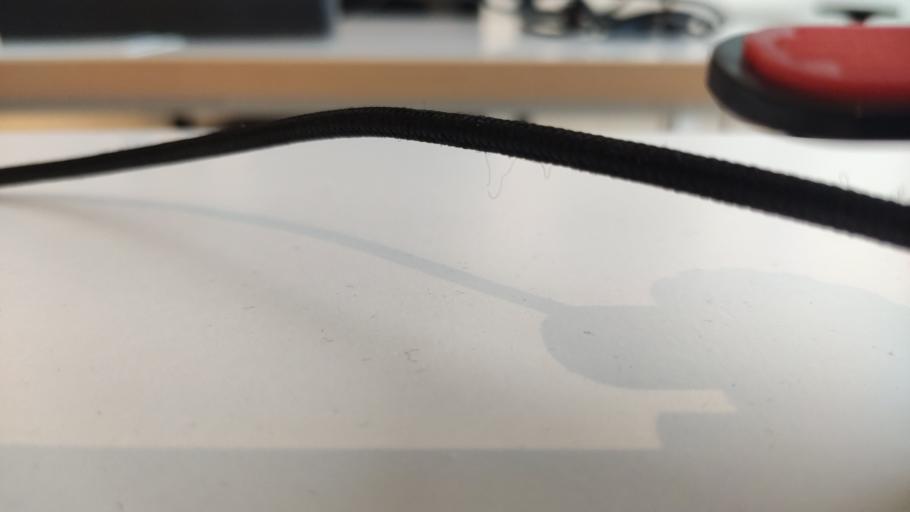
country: RU
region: Moskovskaya
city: Klin
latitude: 56.3596
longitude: 36.7553
